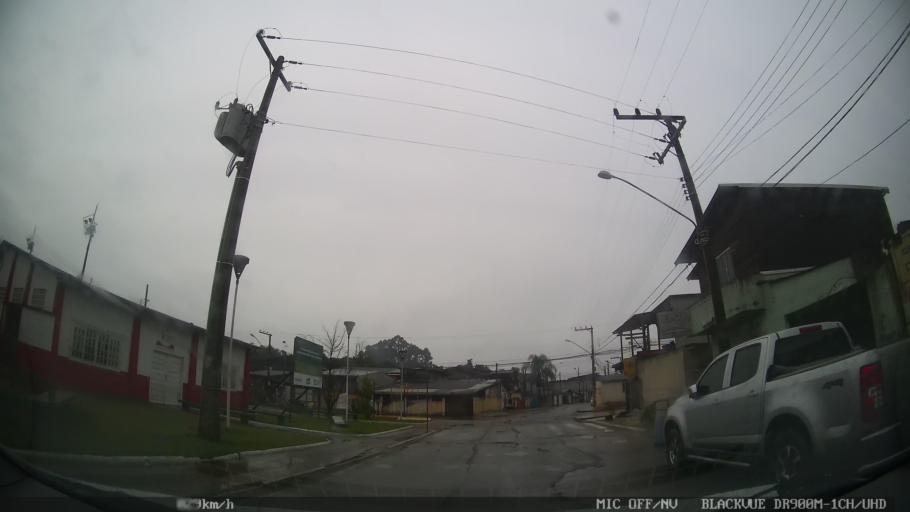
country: BR
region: Santa Catarina
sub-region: Itajai
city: Itajai
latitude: -26.9206
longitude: -48.6902
